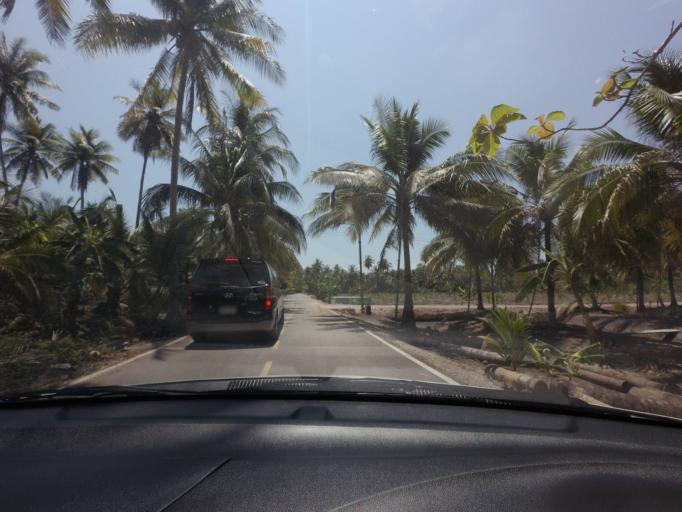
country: TH
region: Samut Songkhram
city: Bang Khon Thi
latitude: 13.4735
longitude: 99.9730
